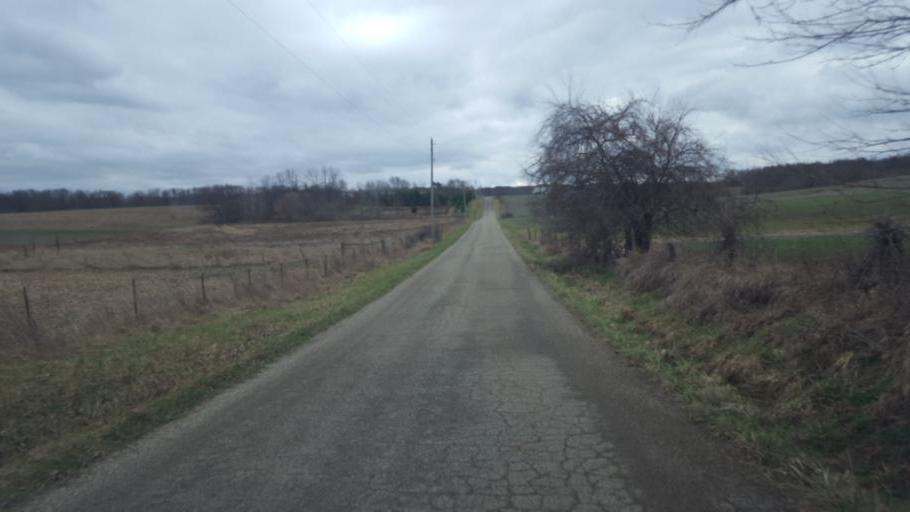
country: US
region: Ohio
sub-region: Knox County
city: Fredericktown
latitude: 40.4218
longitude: -82.6057
